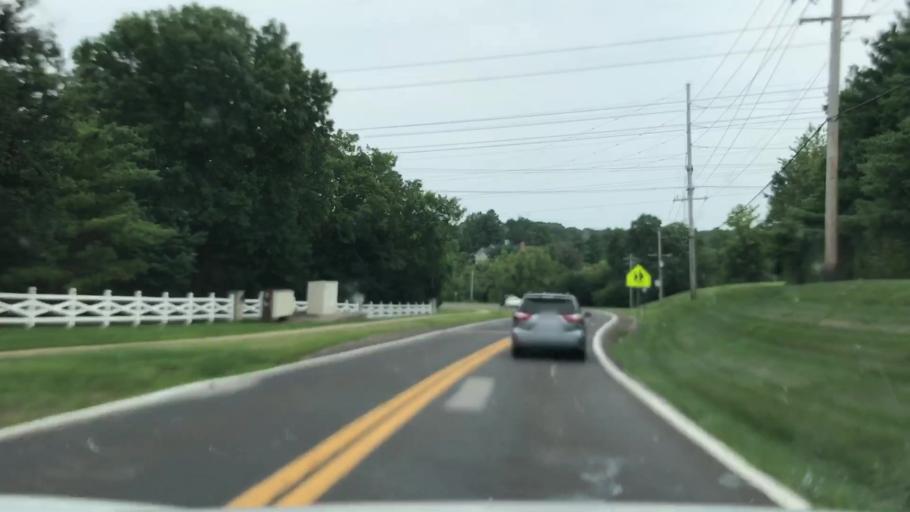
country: US
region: Missouri
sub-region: Saint Louis County
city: Clarkson Valley
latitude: 38.6255
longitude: -90.5912
